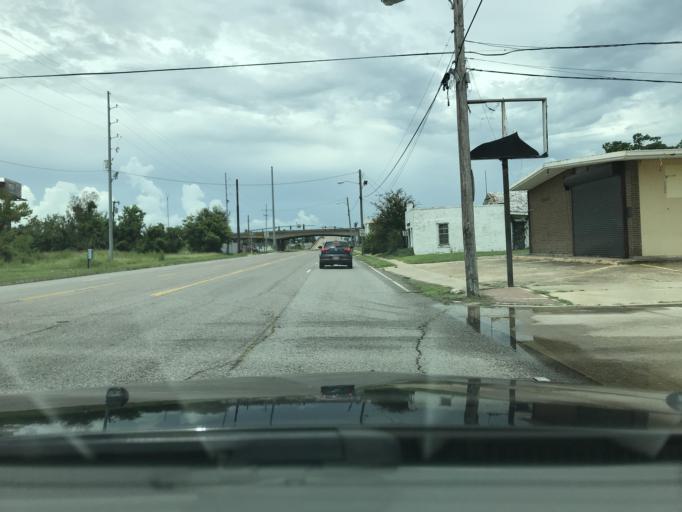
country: US
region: Louisiana
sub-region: Calcasieu Parish
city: Lake Charles
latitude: 30.2341
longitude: -93.2042
